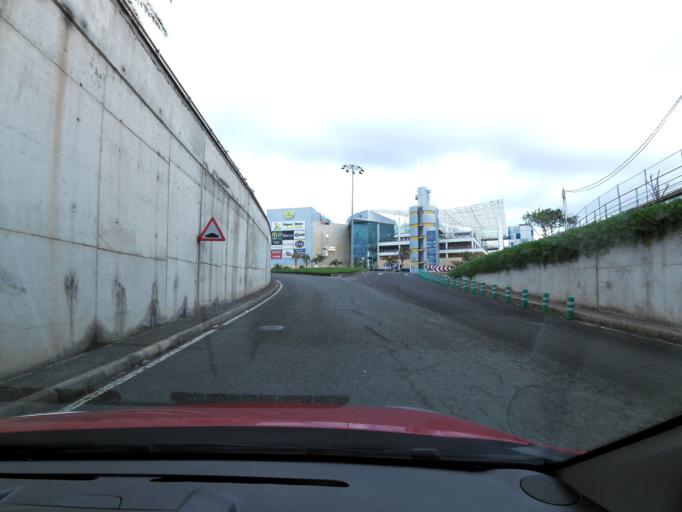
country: ES
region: Canary Islands
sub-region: Provincia de Las Palmas
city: Las Palmas de Gran Canaria
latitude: 28.1403
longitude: -15.4291
